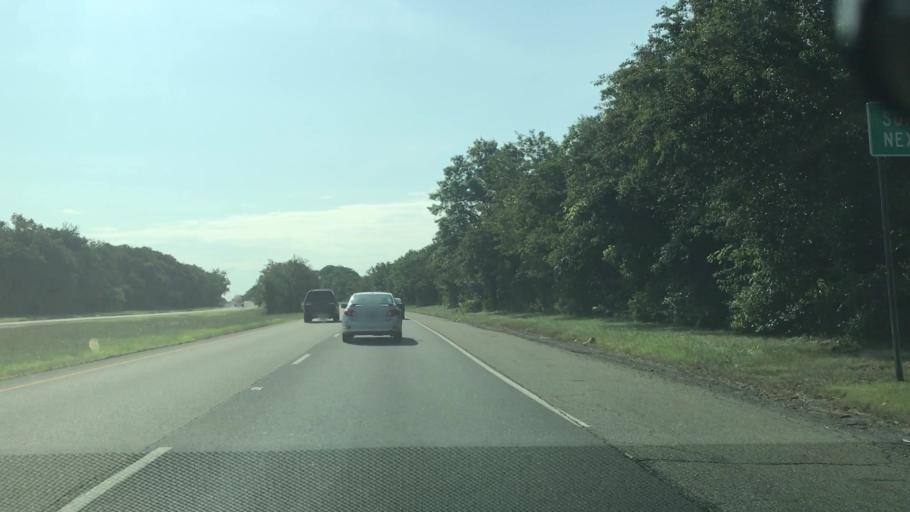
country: US
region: New Jersey
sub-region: Somerset County
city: Bridgewater
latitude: 40.5949
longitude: -74.6685
